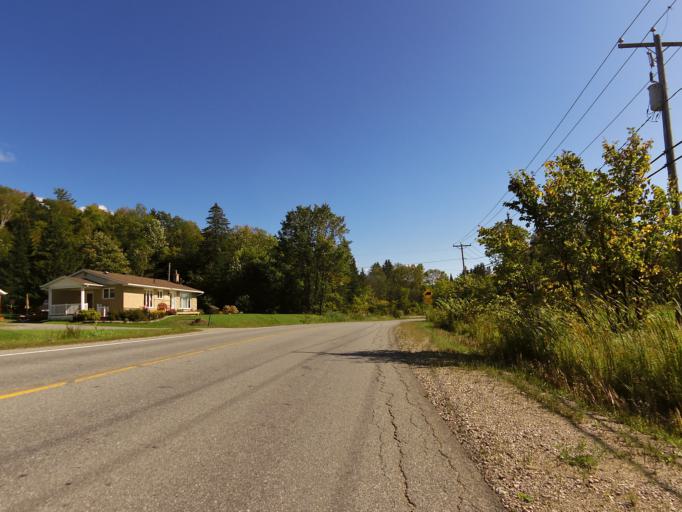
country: CA
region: Ontario
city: Clarence-Rockland
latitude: 45.6558
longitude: -75.4436
